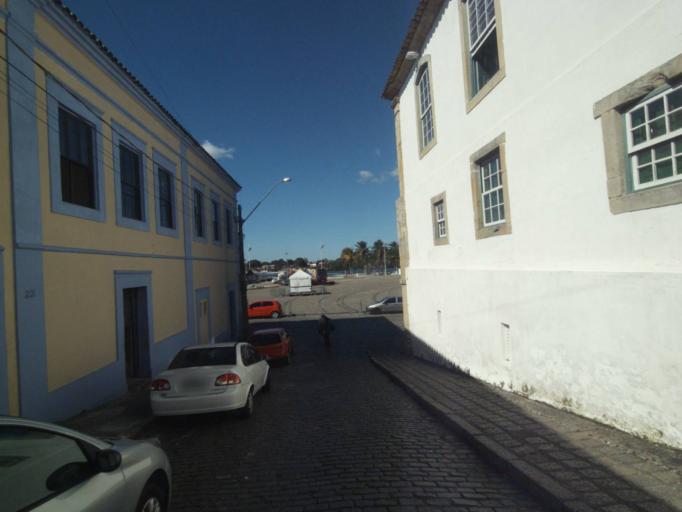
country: BR
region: Parana
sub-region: Paranagua
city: Paranagua
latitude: -25.5214
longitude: -48.5069
